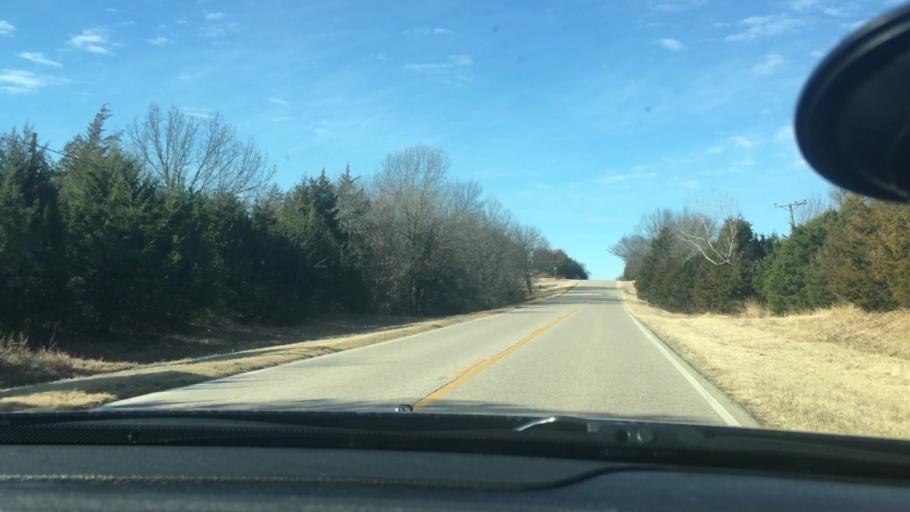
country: US
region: Oklahoma
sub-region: Garvin County
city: Stratford
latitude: 34.9860
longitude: -96.9533
